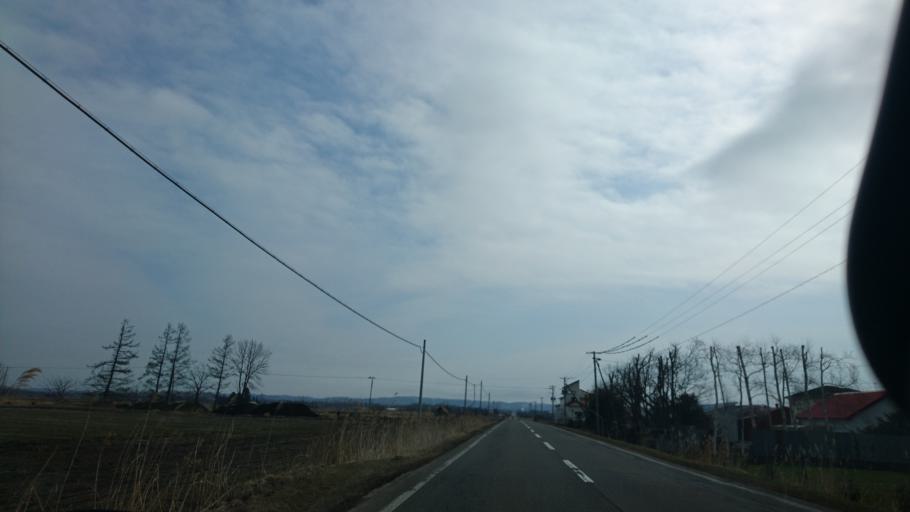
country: JP
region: Hokkaido
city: Otofuke
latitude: 43.0392
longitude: 143.2265
